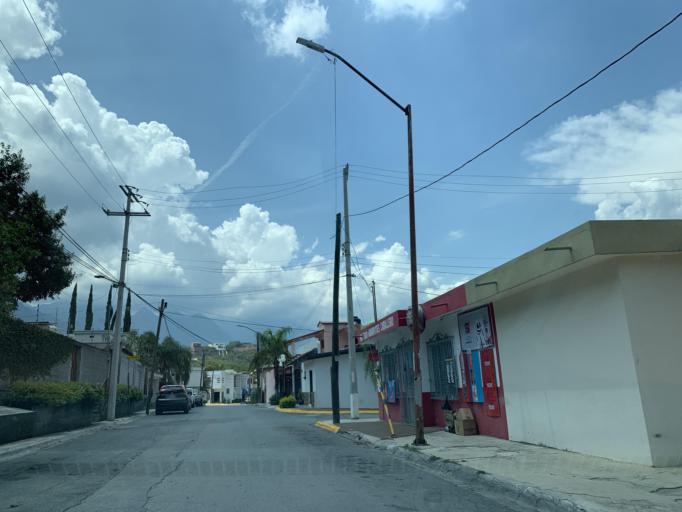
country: MX
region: Nuevo Leon
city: Santiago
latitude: 25.3989
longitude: -100.1283
